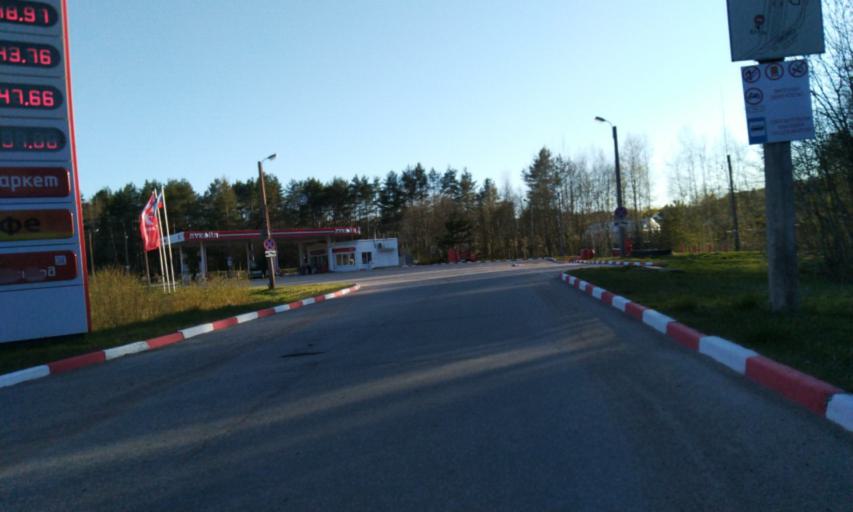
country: RU
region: Leningrad
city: Toksovo
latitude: 60.1366
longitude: 30.5279
